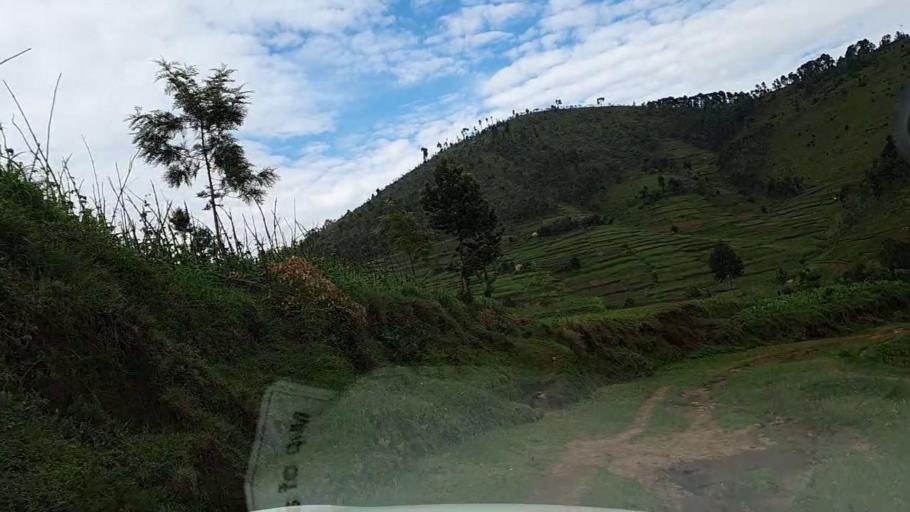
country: RW
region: Southern Province
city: Nzega
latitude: -2.4057
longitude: 29.4978
